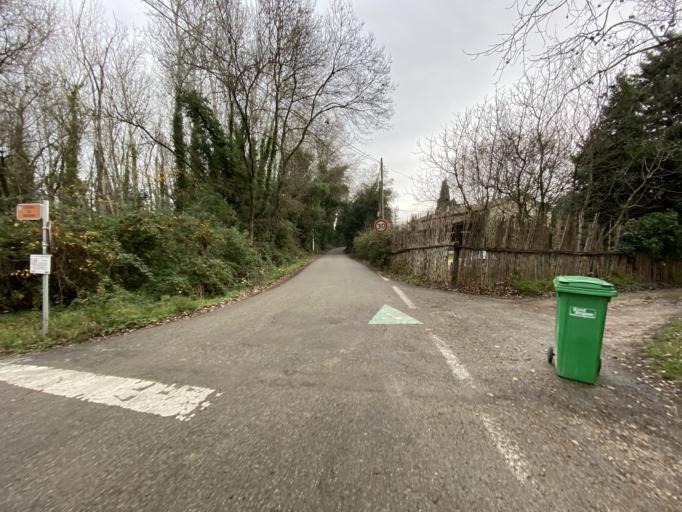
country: FR
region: Provence-Alpes-Cote d'Azur
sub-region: Departement du Vaucluse
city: Avignon
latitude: 43.9557
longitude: 4.8142
